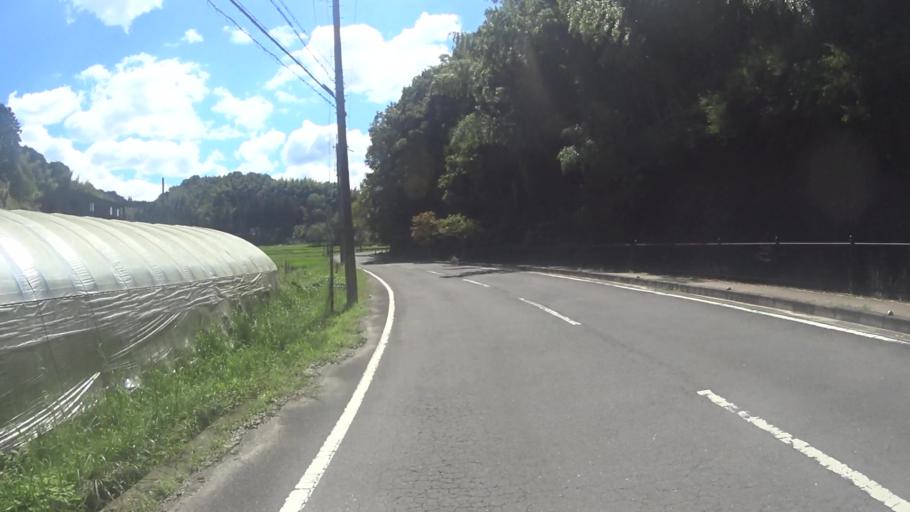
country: JP
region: Nara
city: Nara-shi
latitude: 34.7680
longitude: 135.8776
